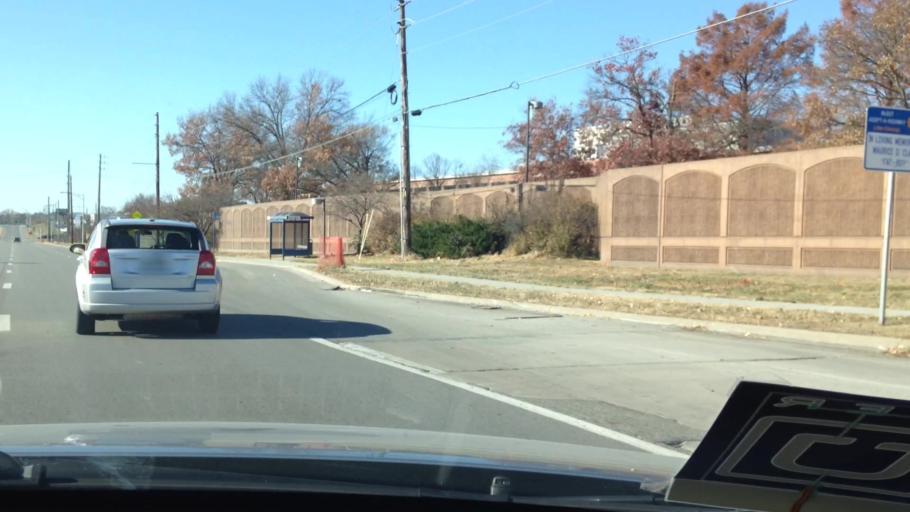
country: US
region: Kansas
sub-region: Johnson County
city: Leawood
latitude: 38.9552
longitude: -94.5729
